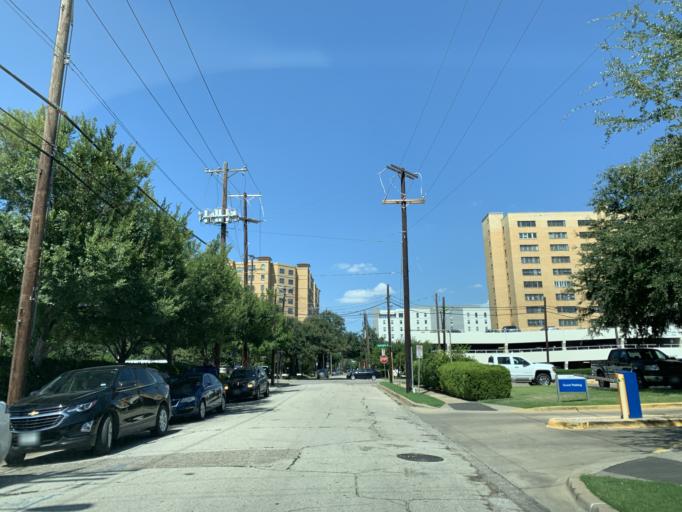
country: US
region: Texas
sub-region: Dallas County
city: Dallas
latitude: 32.7922
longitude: -96.7805
